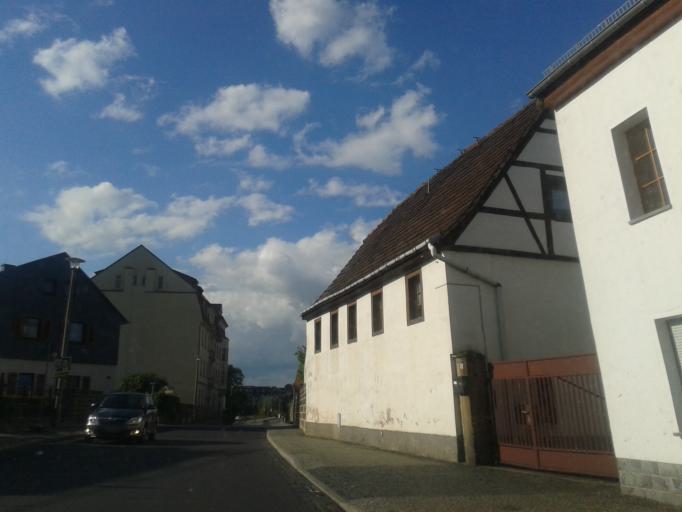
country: DE
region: Saxony
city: Dresden
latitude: 51.0727
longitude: 13.6991
